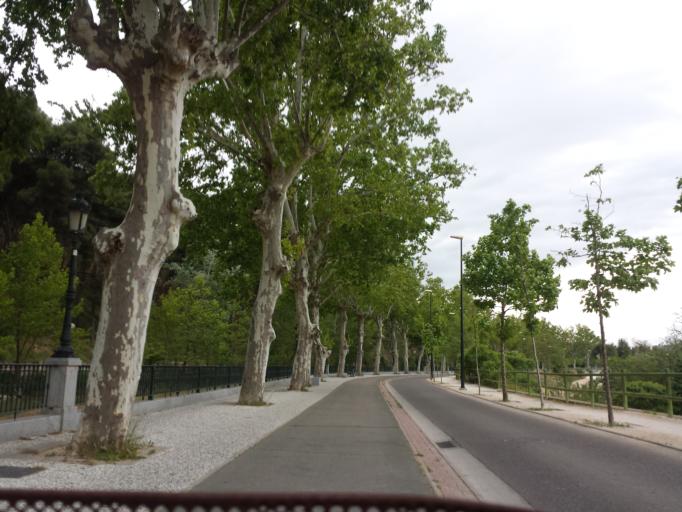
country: ES
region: Aragon
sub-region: Provincia de Zaragoza
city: Delicias
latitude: 41.6237
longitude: -0.9015
